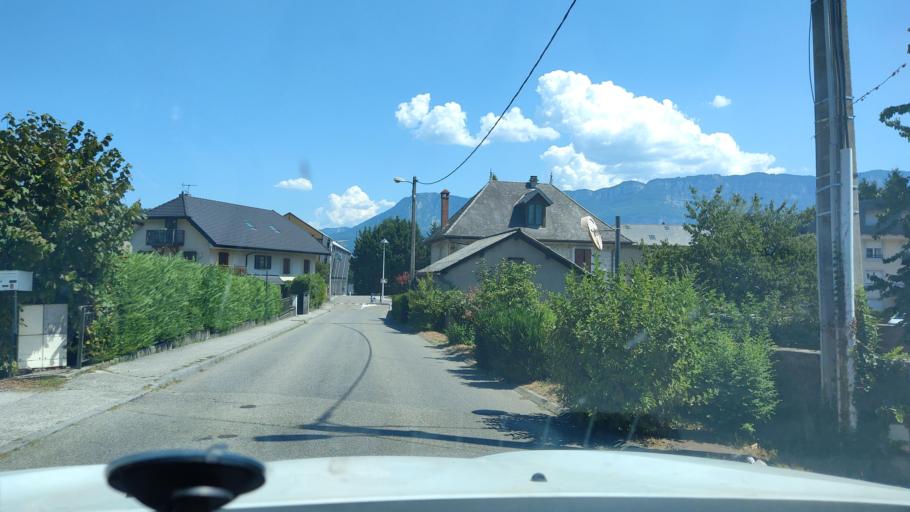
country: FR
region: Rhone-Alpes
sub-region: Departement de la Savoie
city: Le Bourget-du-Lac
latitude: 45.6441
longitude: 5.8606
